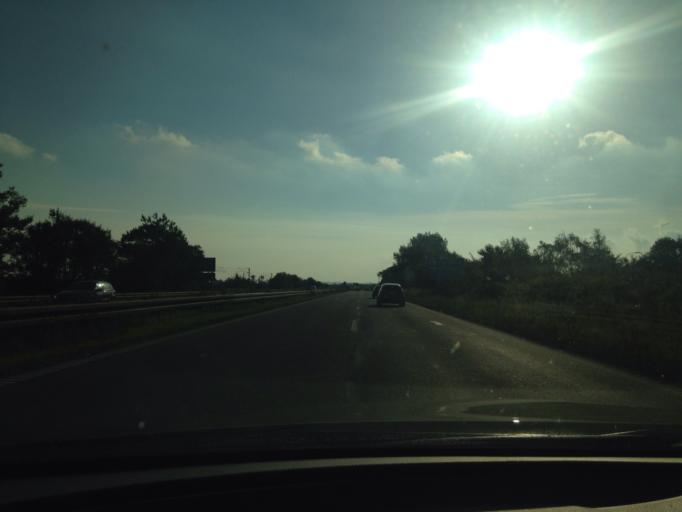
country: DK
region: Zealand
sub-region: Slagelse Kommune
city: Forlev
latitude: 55.3624
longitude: 11.2150
